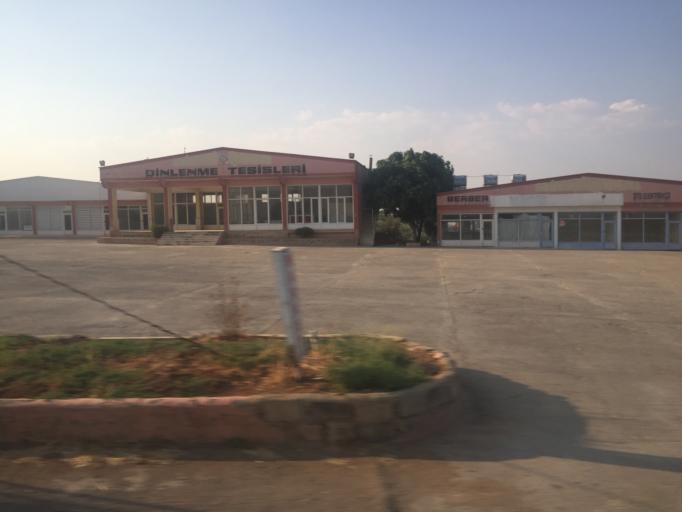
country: TR
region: Sanliurfa
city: Birecik
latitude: 37.0223
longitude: 37.9149
